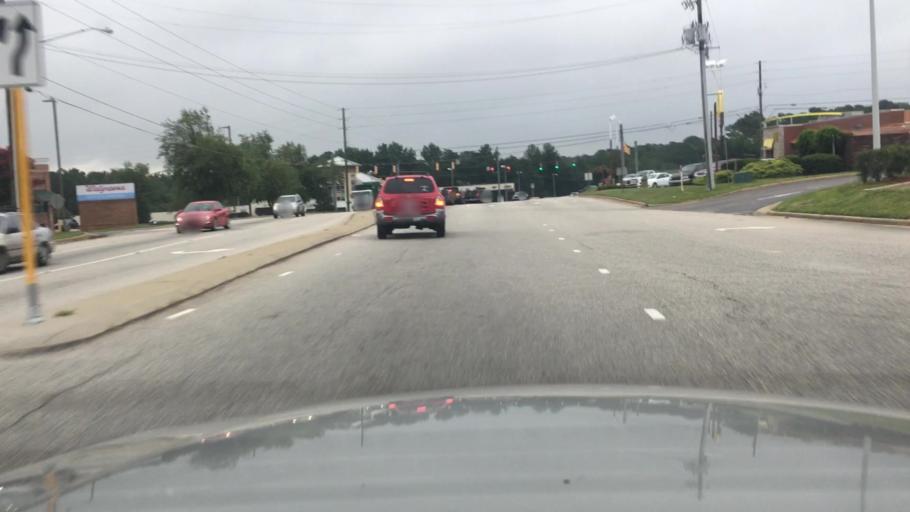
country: US
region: North Carolina
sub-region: Cumberland County
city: Hope Mills
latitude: 34.9853
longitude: -78.9664
